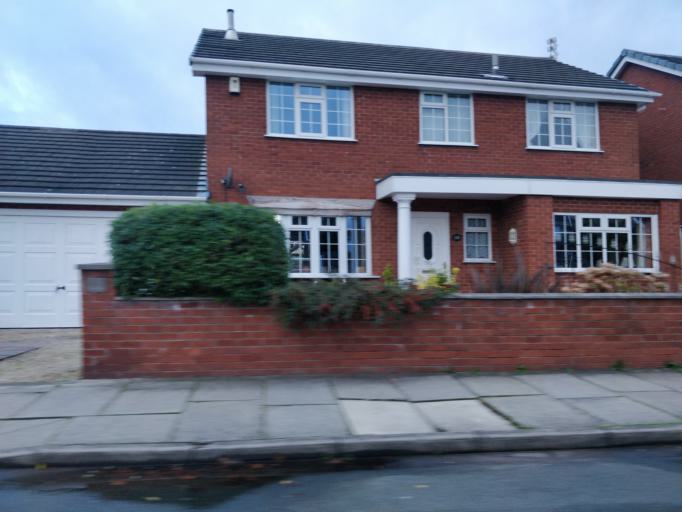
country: GB
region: England
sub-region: Sefton
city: Southport
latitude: 53.6671
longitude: -2.9781
